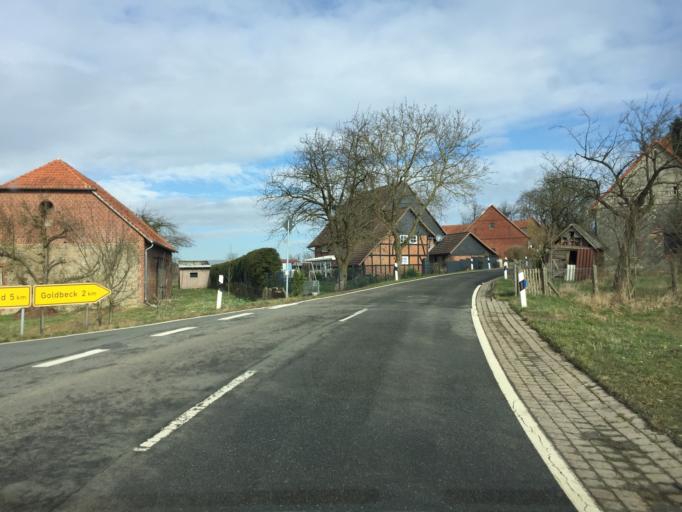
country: DE
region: Lower Saxony
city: Aerzen
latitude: 52.0935
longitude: 9.1655
